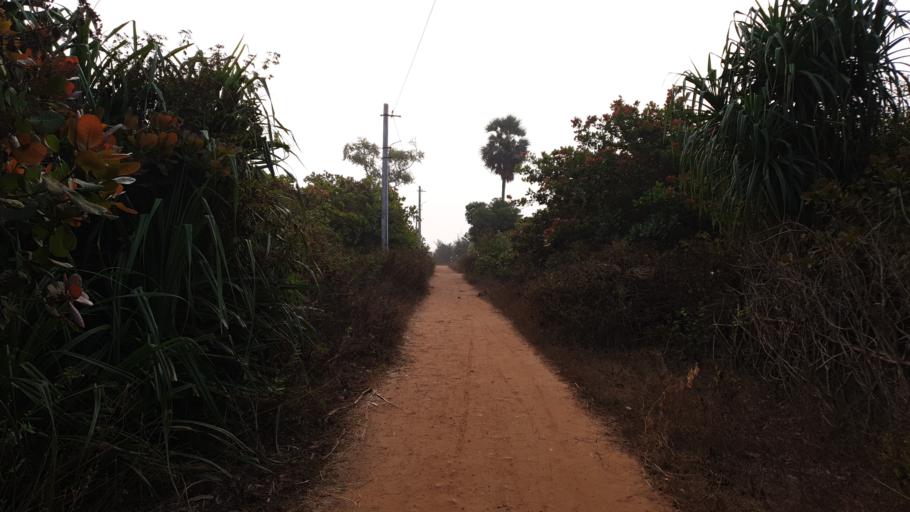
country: IN
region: Andhra Pradesh
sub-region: Srikakulam
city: Palasa
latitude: 18.6893
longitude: 84.4472
